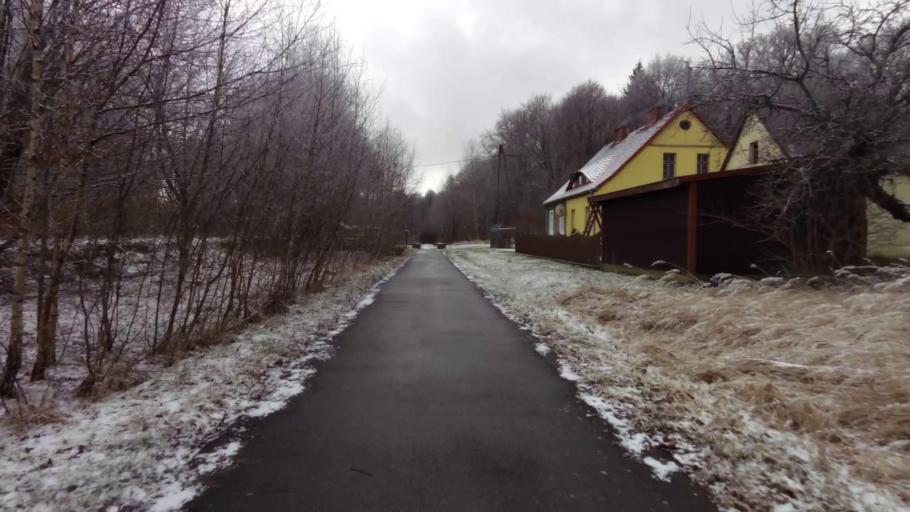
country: PL
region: West Pomeranian Voivodeship
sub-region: Powiat swidwinski
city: Polczyn-Zdroj
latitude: 53.6652
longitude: 16.0292
